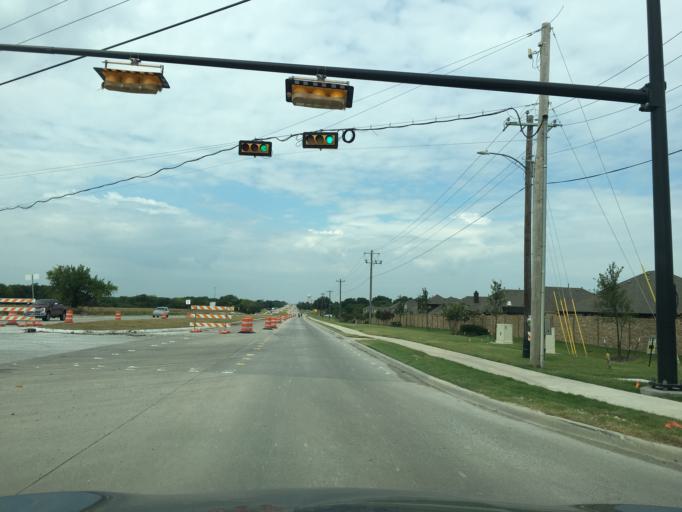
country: US
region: Texas
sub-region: Collin County
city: Melissa
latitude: 33.2924
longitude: -96.5464
